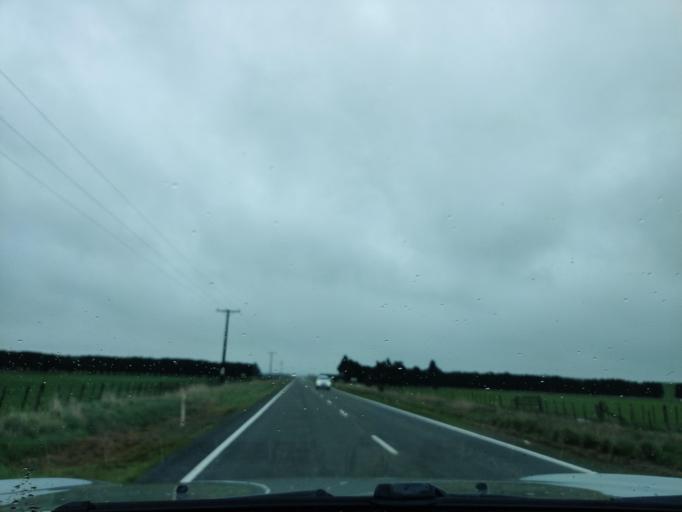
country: NZ
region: Hawke's Bay
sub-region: Hastings District
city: Hastings
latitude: -40.0201
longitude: 176.2893
